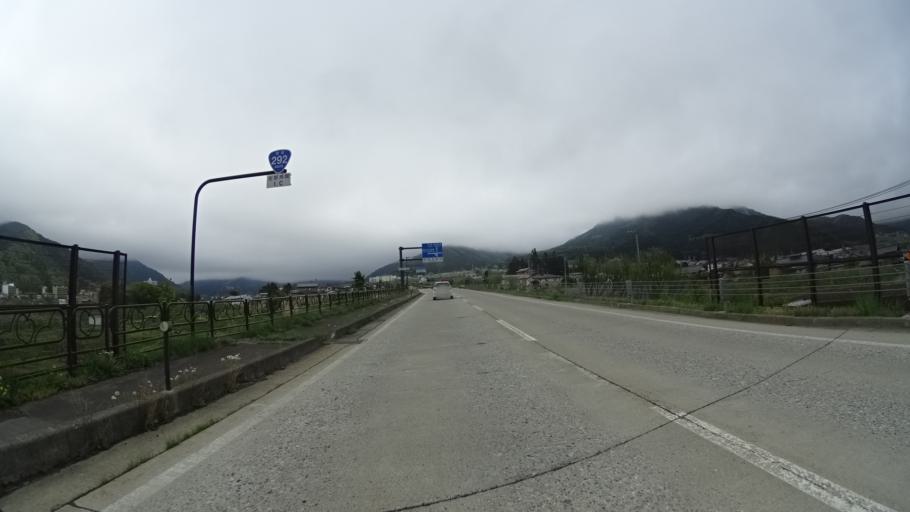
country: JP
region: Nagano
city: Nakano
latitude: 36.7375
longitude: 138.4102
